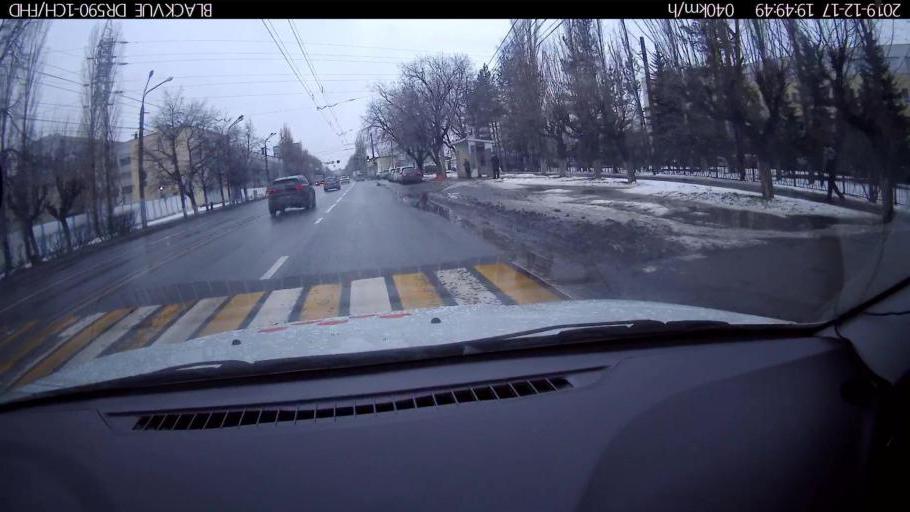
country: RU
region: Nizjnij Novgorod
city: Nizhniy Novgorod
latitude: 56.3302
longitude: 43.9022
